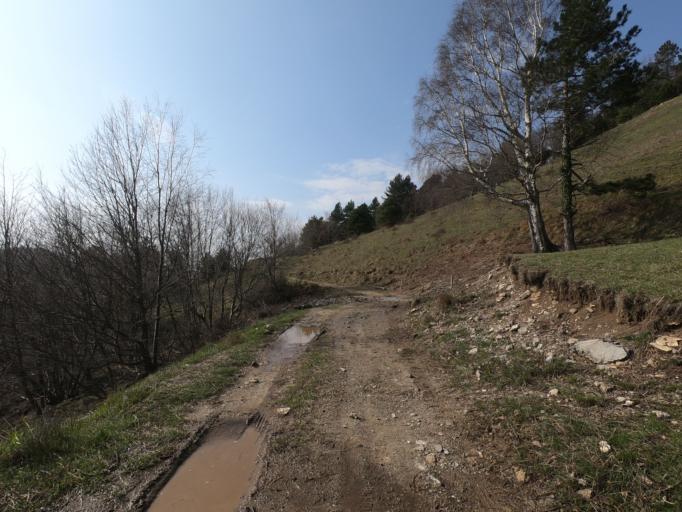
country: IT
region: Liguria
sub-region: Provincia di Savona
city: Castelvecchio di Rocca Barbena
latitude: 44.1278
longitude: 8.1429
